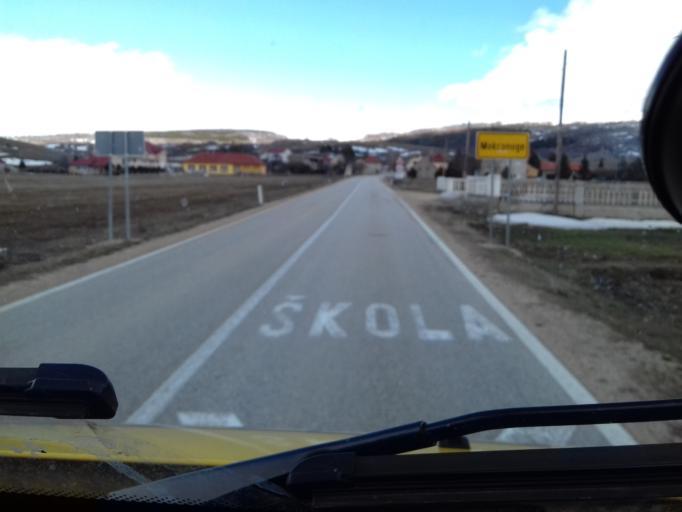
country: BA
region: Federation of Bosnia and Herzegovina
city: Tomislavgrad
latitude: 43.7599
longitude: 17.2347
